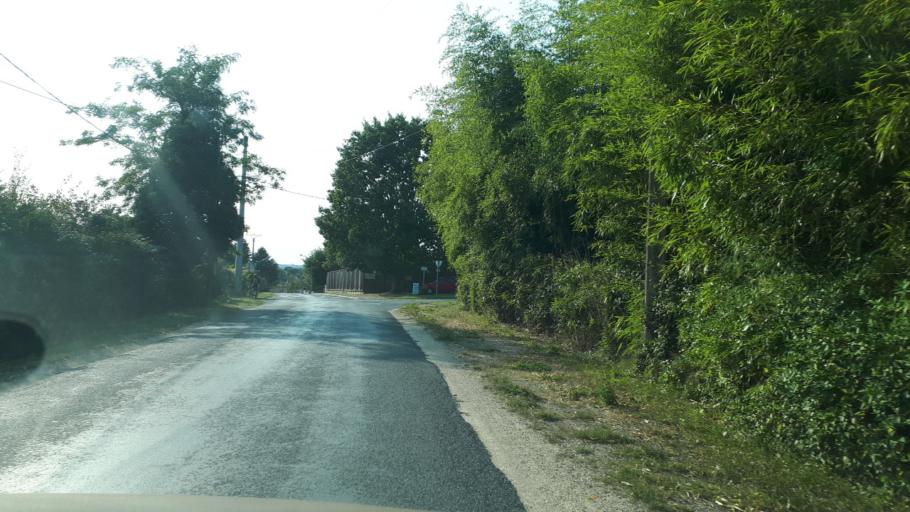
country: FR
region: Centre
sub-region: Departement du Cher
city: Saint-Eloy-de-Gy
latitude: 47.2239
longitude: 2.3277
